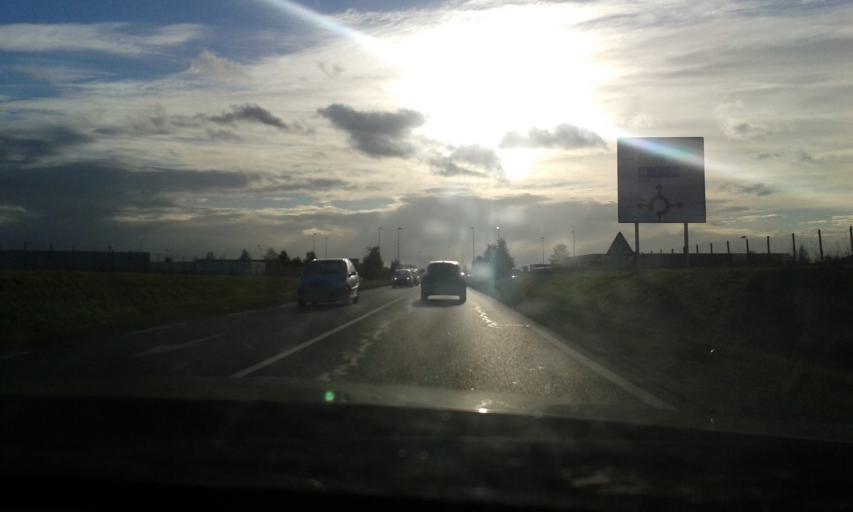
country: FR
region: Centre
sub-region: Departement d'Eure-et-Loir
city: Mainvilliers
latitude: 48.4484
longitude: 1.4405
